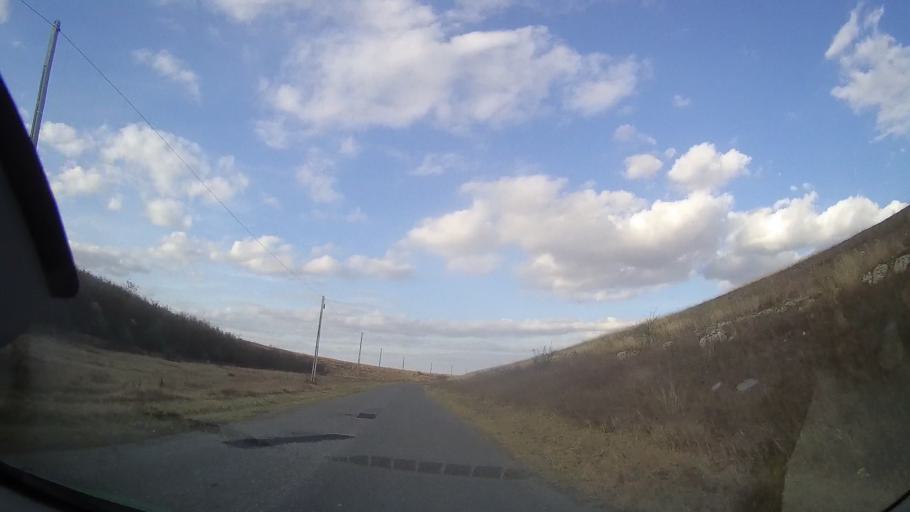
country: RO
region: Constanta
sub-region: Comuna Cerchezu
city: Cerchezu
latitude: 43.8364
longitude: 28.0975
